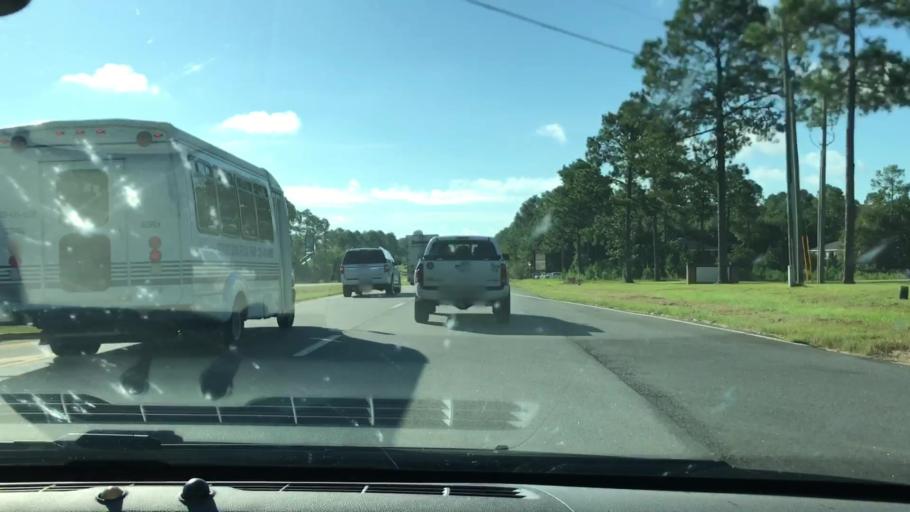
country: US
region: Georgia
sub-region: Lee County
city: Leesburg
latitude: 31.6472
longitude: -84.2601
